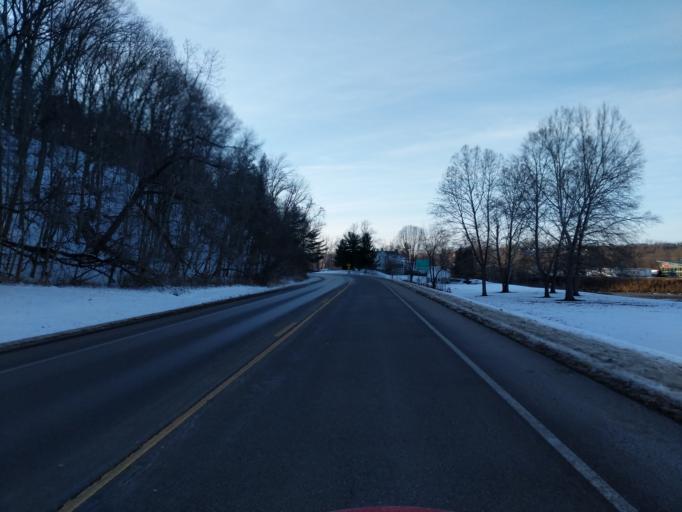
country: US
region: Ohio
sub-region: Athens County
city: Athens
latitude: 39.3284
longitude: -82.1227
